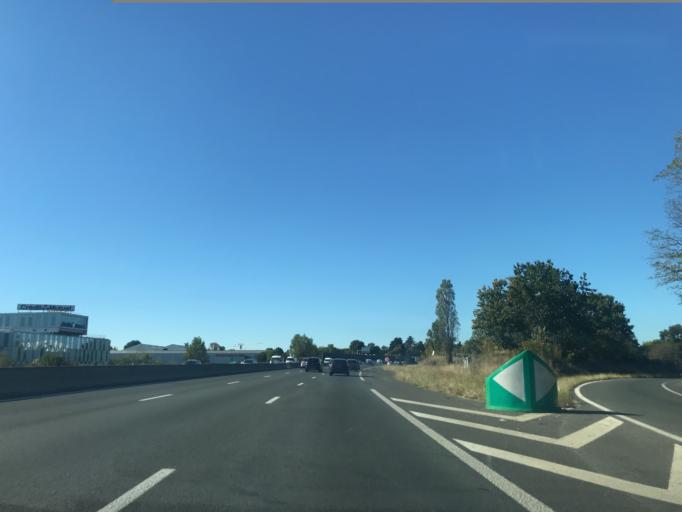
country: FR
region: Aquitaine
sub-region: Departement de la Gironde
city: Pessac
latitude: 44.7893
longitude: -0.6447
